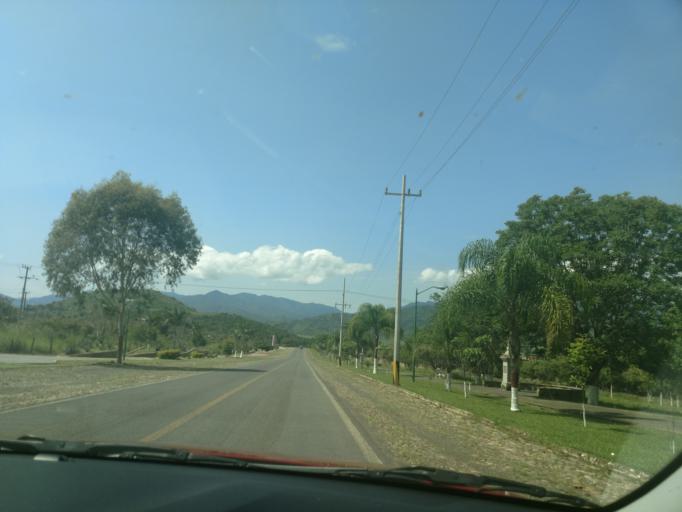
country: MX
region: Jalisco
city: Talpa de Allende
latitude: 20.3984
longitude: -104.8159
